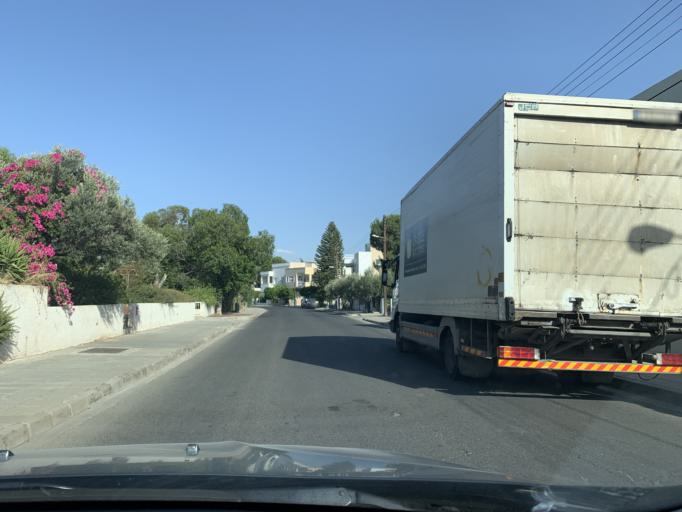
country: CY
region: Lefkosia
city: Nicosia
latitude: 35.1522
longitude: 33.3870
